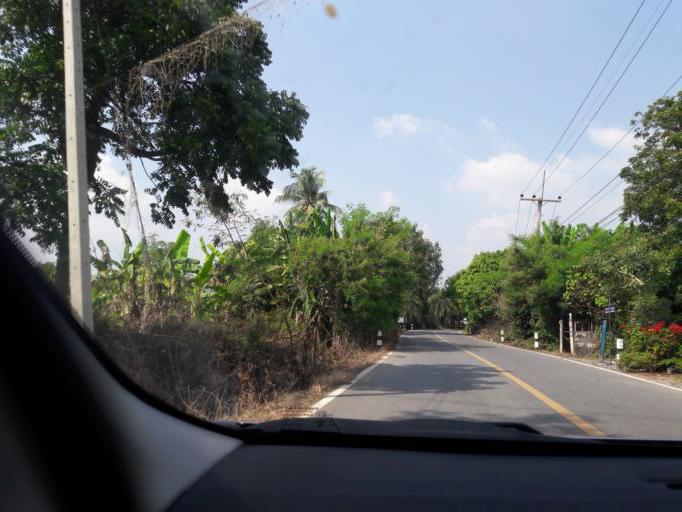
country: TH
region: Ang Thong
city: Ang Thong
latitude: 14.5570
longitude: 100.4273
